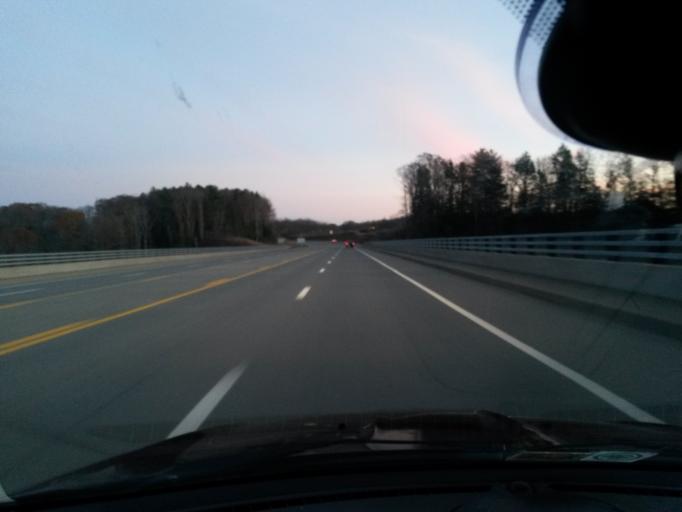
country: US
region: West Virginia
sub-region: Raleigh County
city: Beckley
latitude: 37.7915
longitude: -81.1645
